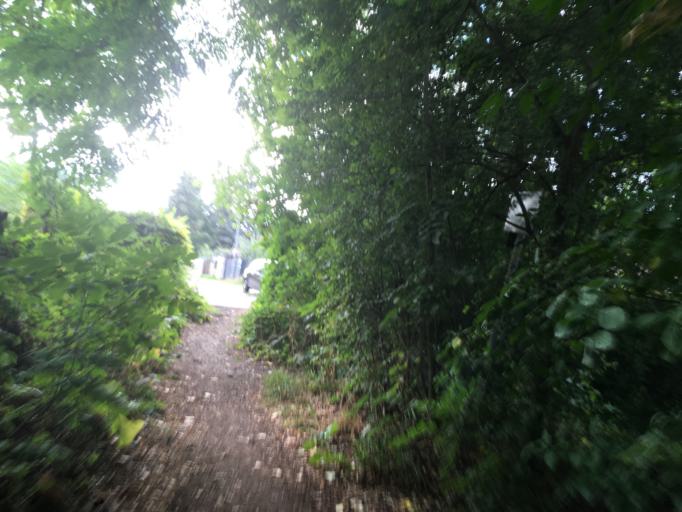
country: DE
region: Berlin
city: Weissensee
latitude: 52.5641
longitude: 13.4811
